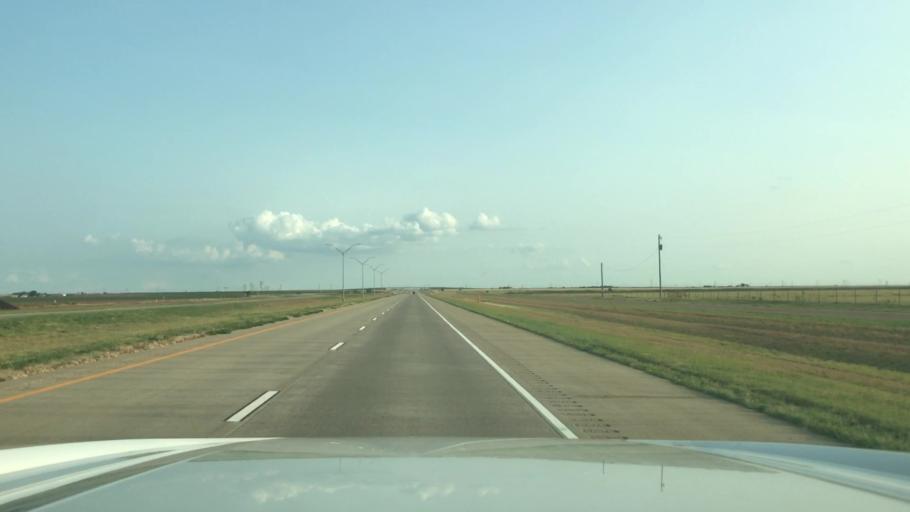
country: US
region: Texas
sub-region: Swisher County
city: Tulia
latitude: 34.4645
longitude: -101.7772
